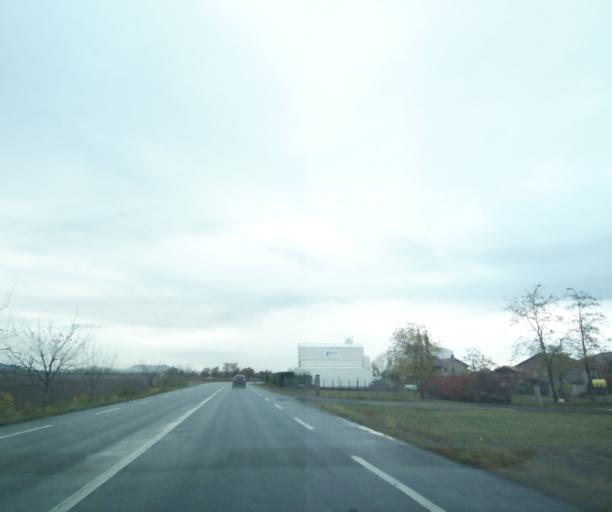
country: FR
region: Auvergne
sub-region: Departement du Puy-de-Dome
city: Perignat-les-Sarlieve
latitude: 45.7580
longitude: 3.1543
